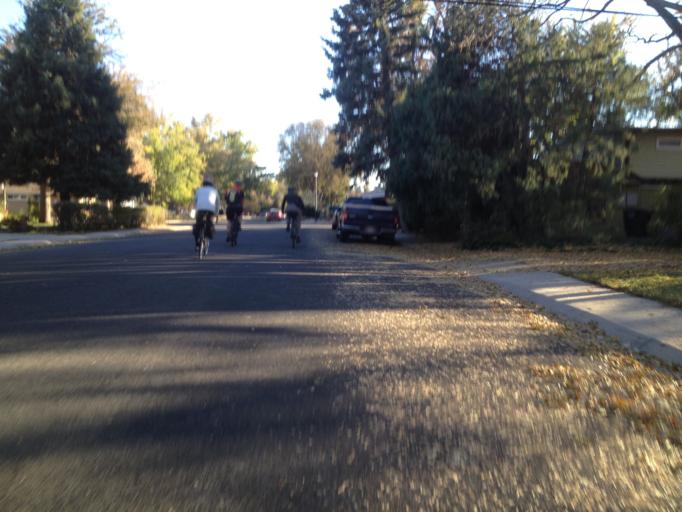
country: US
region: Colorado
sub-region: Boulder County
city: Longmont
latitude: 40.1763
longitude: -105.1143
